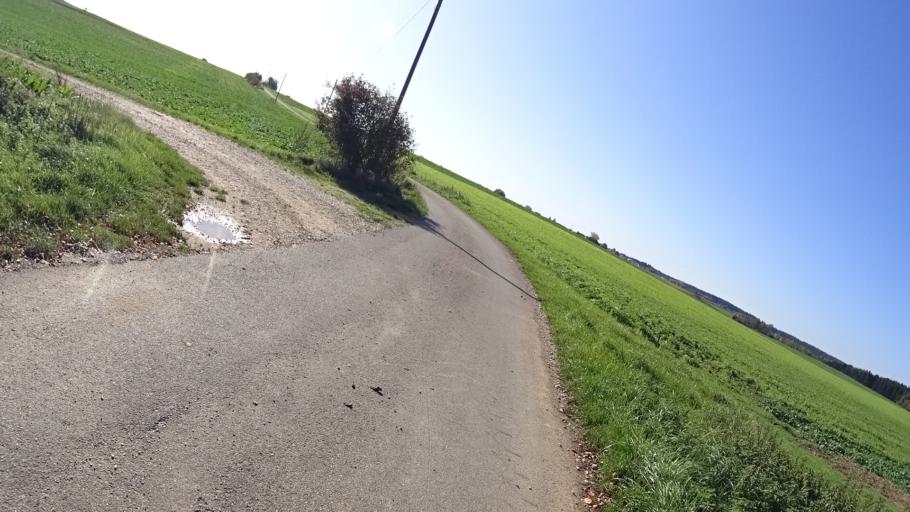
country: DE
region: Bavaria
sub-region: Upper Bavaria
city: Hitzhofen
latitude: 48.8644
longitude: 11.3221
